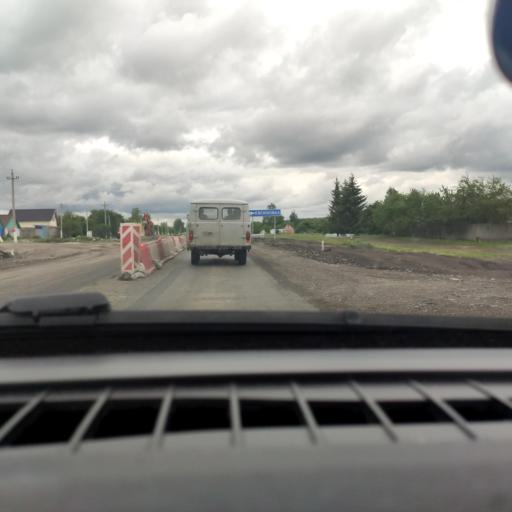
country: RU
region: Lipetsk
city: Usman'
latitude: 51.9526
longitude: 39.7827
